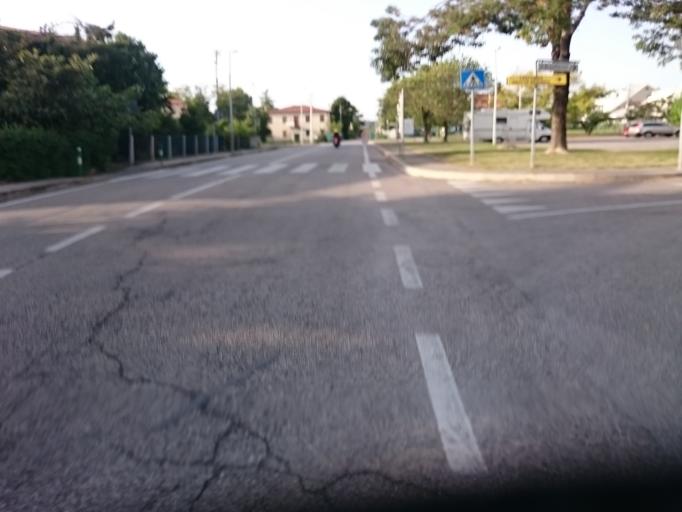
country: IT
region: Veneto
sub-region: Provincia di Padova
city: Padova
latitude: 45.3978
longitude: 11.9034
